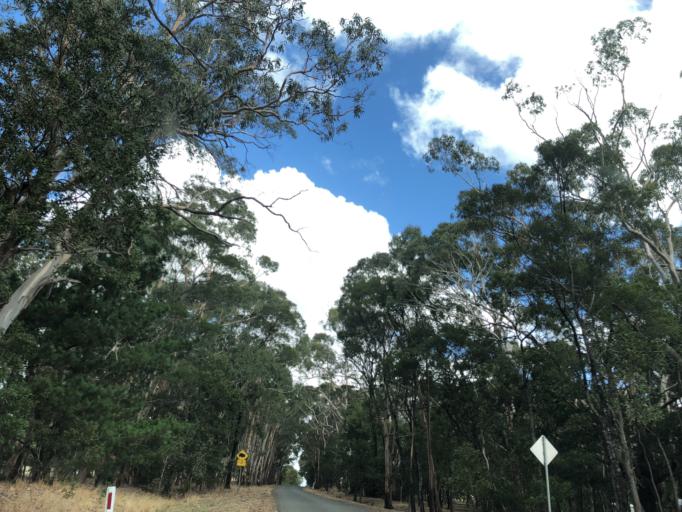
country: AU
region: Victoria
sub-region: Moorabool
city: Bacchus Marsh
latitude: -37.5546
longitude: 144.3495
